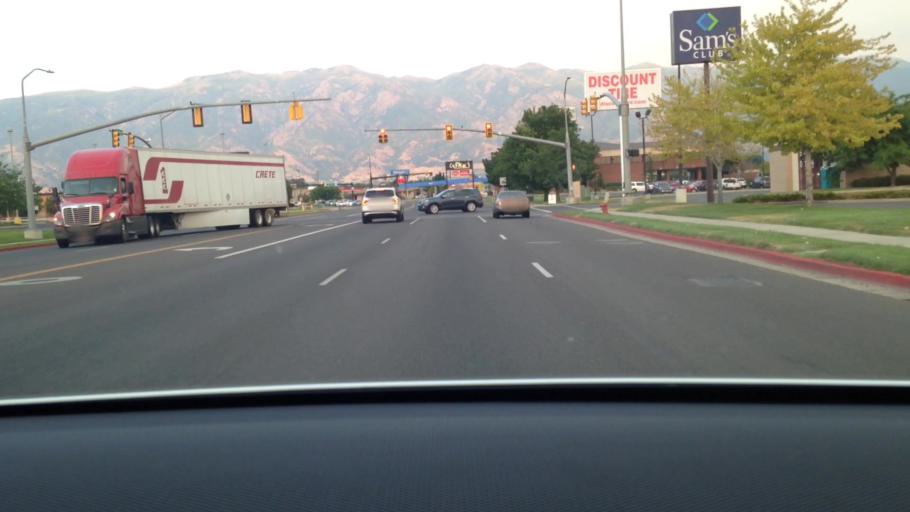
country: US
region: Utah
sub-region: Davis County
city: Layton
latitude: 41.0718
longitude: -111.9835
